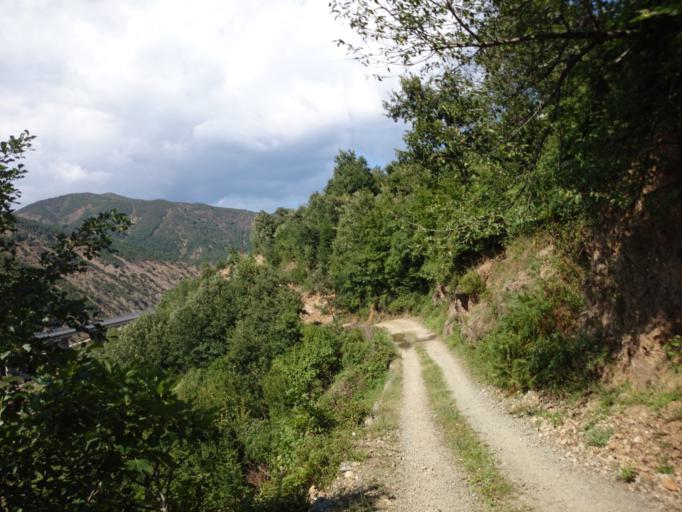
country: AL
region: Lezhe
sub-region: Rrethi i Lezhes
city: Blinisht
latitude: 41.8628
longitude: 20.0190
